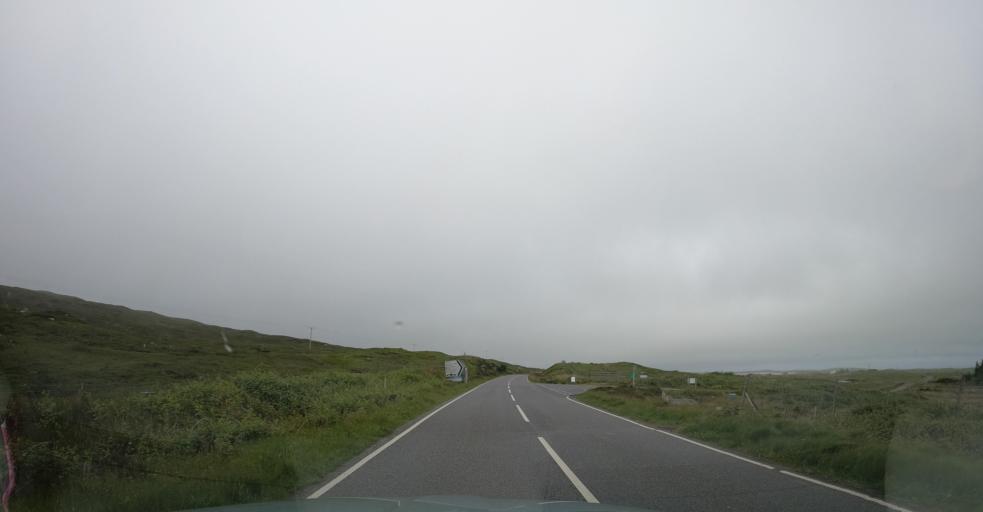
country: GB
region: Scotland
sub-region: Eilean Siar
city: Isle of North Uist
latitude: 57.6469
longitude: -7.2424
